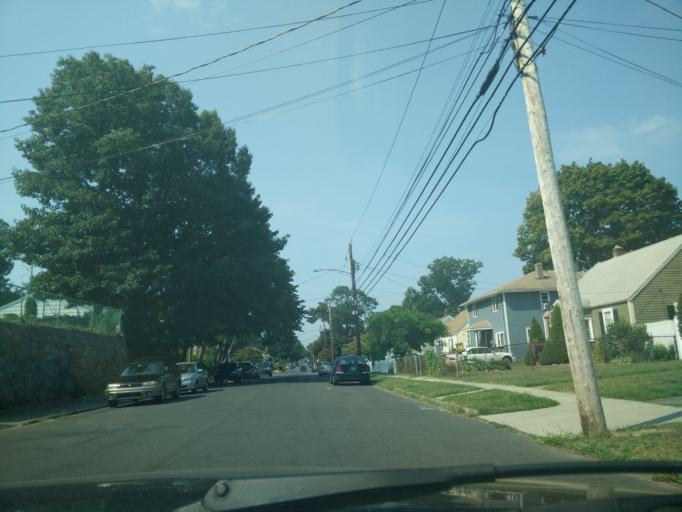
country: US
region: Connecticut
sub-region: Fairfield County
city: Trumbull
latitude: 41.2090
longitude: -73.2120
